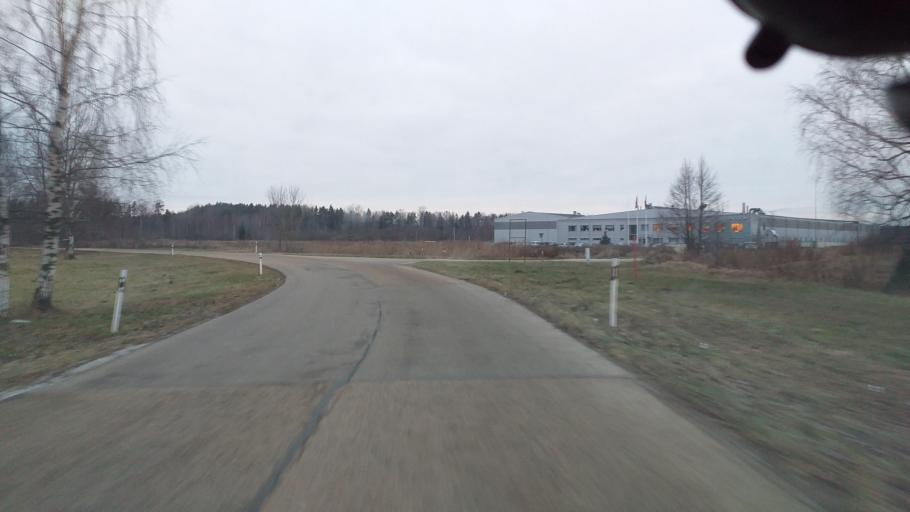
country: LV
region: Olaine
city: Olaine
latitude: 56.8003
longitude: 23.9317
